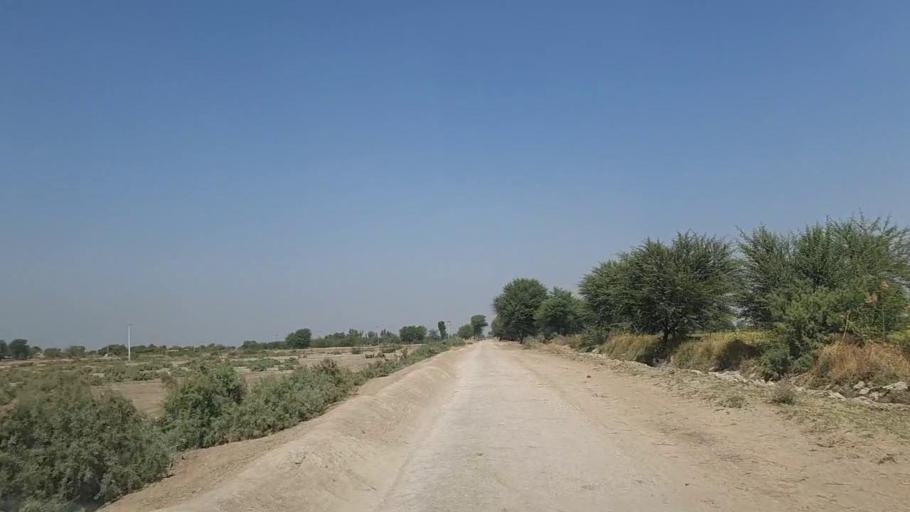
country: PK
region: Sindh
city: Samaro
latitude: 25.2124
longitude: 69.4042
